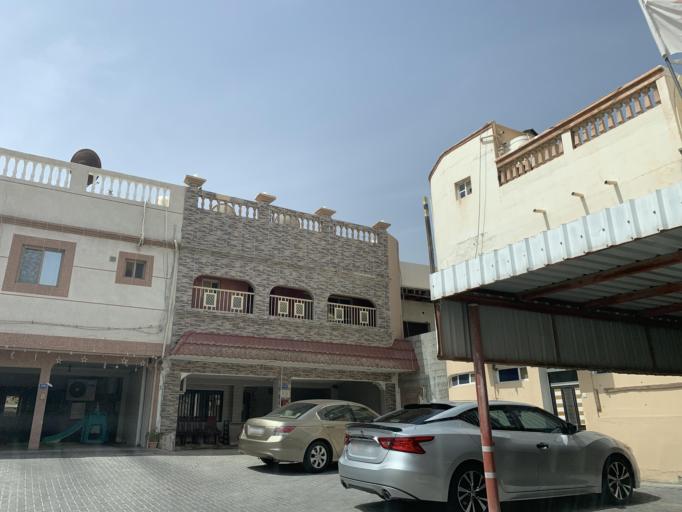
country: BH
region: Northern
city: Madinat `Isa
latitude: 26.1681
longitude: 50.5623
